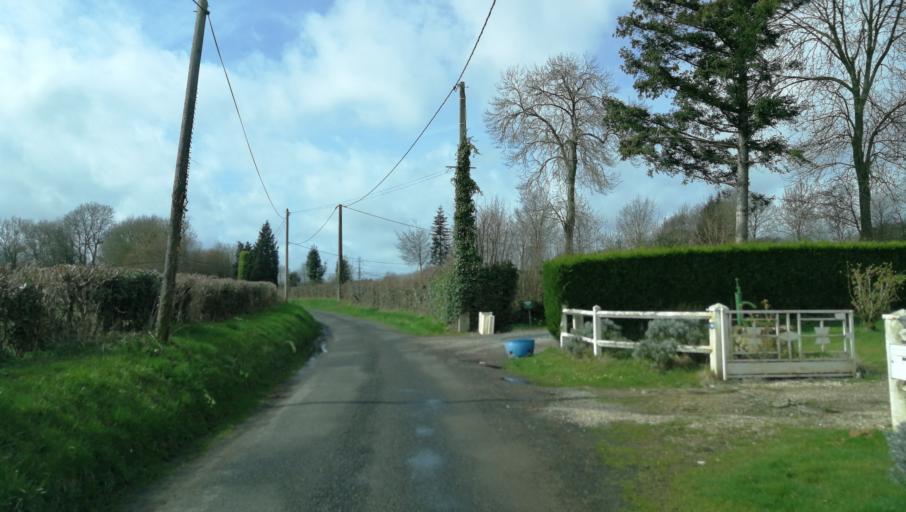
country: FR
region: Haute-Normandie
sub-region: Departement de l'Eure
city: Lieurey
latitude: 49.2388
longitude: 0.4820
